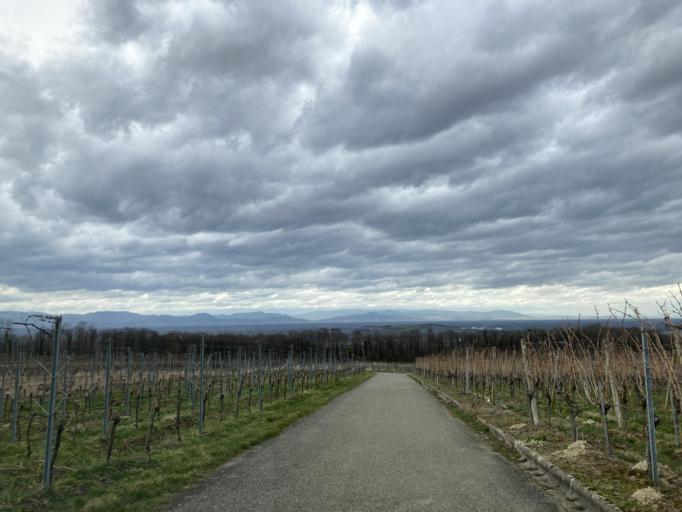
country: DE
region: Baden-Wuerttemberg
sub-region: Freiburg Region
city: Vogtsburg
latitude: 48.1150
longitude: 7.6446
